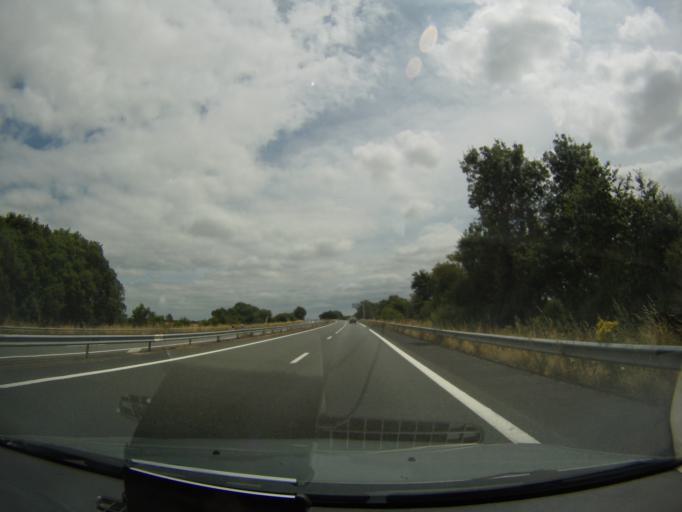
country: FR
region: Pays de la Loire
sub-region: Departement de Maine-et-Loire
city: Tillieres
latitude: 47.1404
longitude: -1.1709
